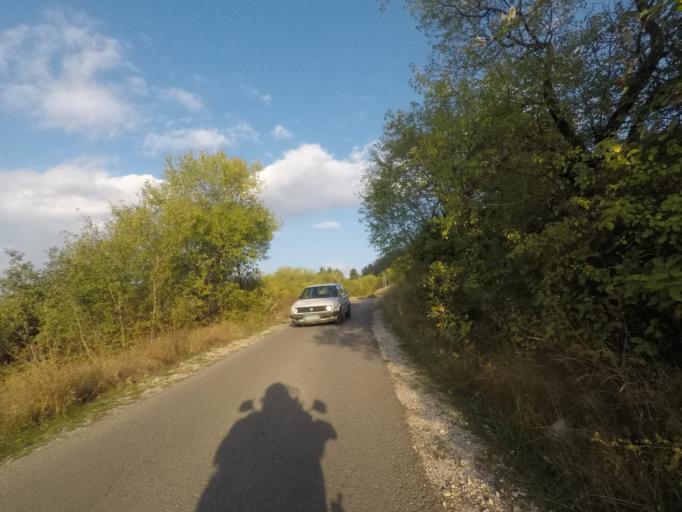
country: ME
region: Kotor
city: Kotor
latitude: 42.4232
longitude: 18.8047
